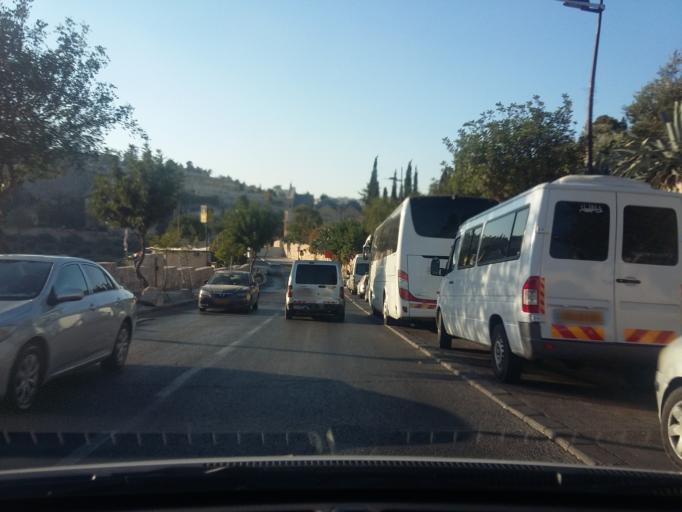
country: PS
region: West Bank
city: Old City
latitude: 31.7777
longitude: 35.2400
